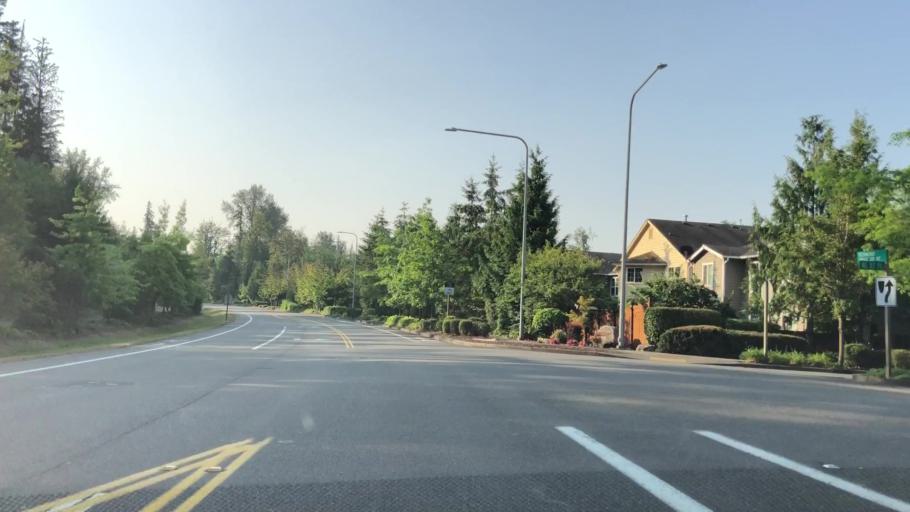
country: US
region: Washington
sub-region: King County
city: Union Hill-Novelty Hill
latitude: 47.6802
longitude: -122.0329
